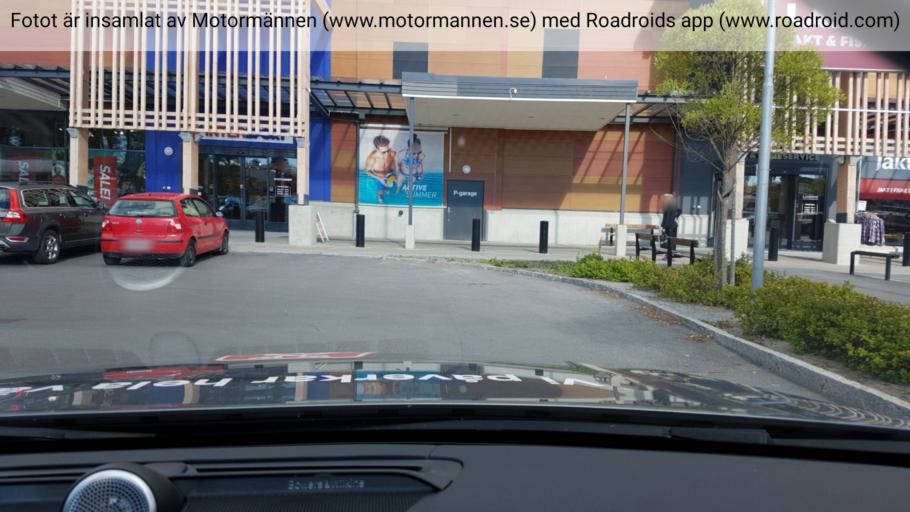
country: SE
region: Jaemtland
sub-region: OEstersunds Kommun
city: Ostersund
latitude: 63.1713
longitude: 14.6906
